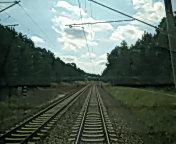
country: DE
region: Brandenburg
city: Halbe
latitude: 52.1001
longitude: 13.7116
